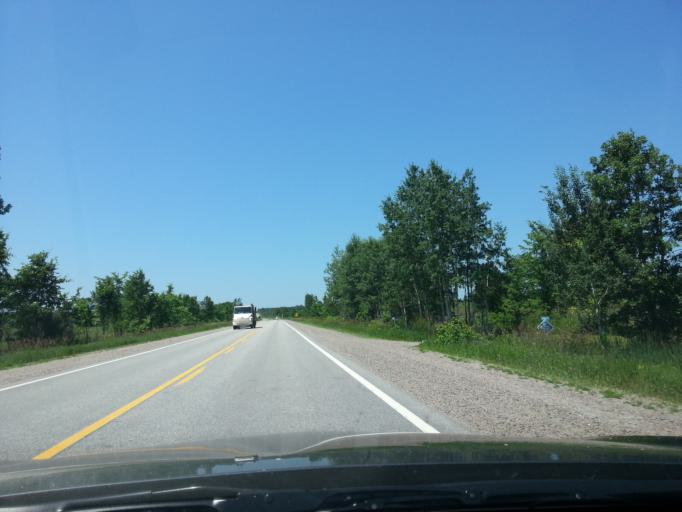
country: CA
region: Ontario
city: Arnprior
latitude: 45.5265
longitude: -76.2587
